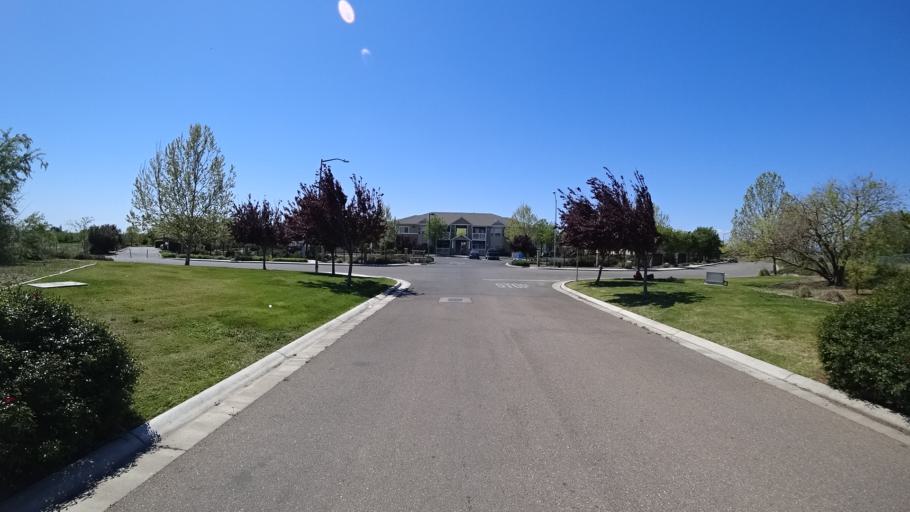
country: US
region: California
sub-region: Glenn County
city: Orland
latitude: 39.7454
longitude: -122.1728
